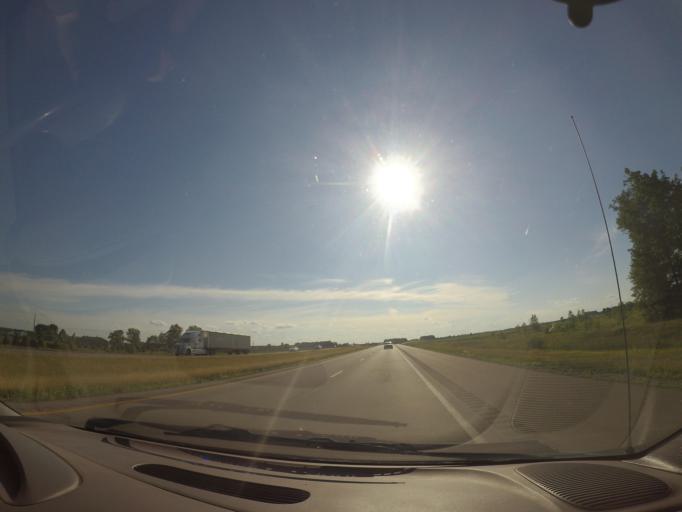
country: US
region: Ohio
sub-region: Henry County
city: Liberty Center
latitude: 41.4292
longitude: -83.9967
